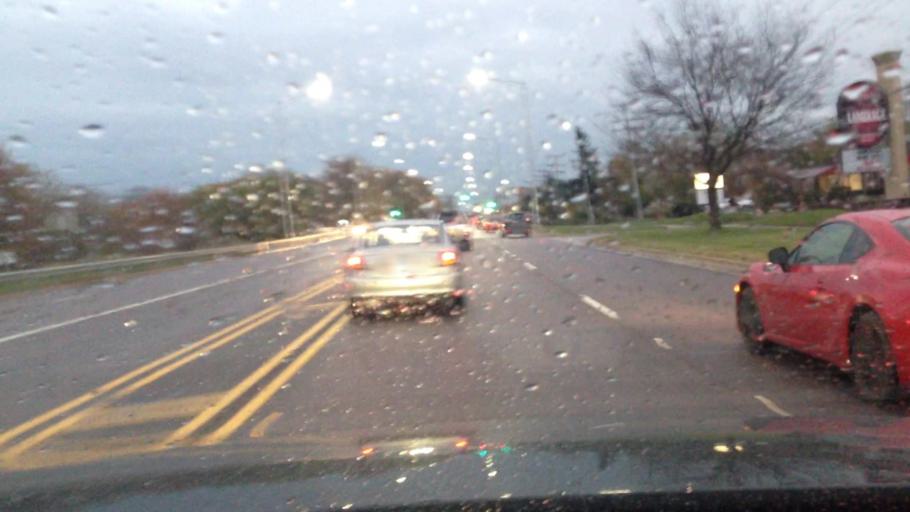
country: US
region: Illinois
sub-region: Cook County
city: Rolling Meadows
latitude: 42.0606
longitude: -88.0183
